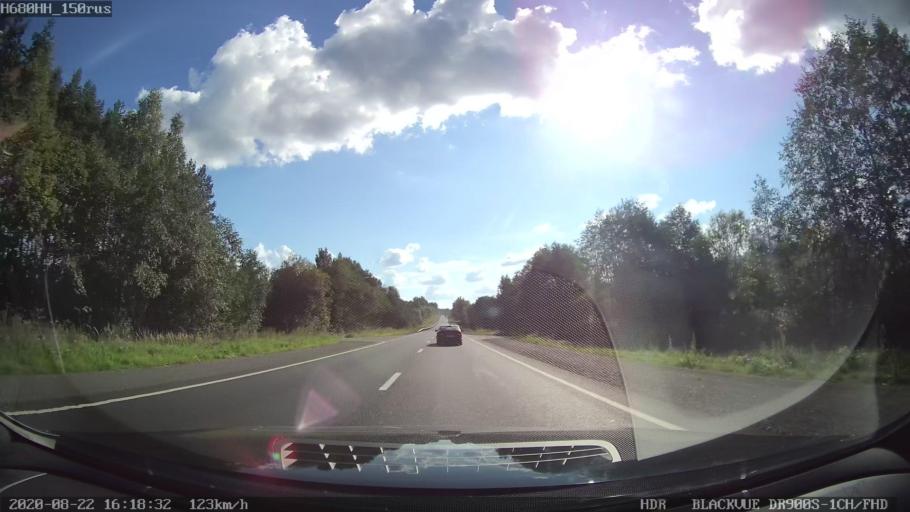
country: RU
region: Tverskaya
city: Rameshki
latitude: 57.4151
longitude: 36.1382
